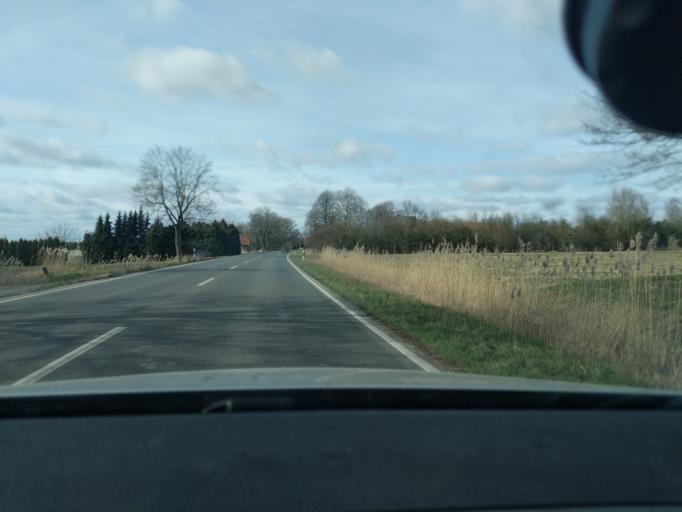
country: DE
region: Lower Saxony
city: Drochtersen
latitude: 53.6955
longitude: 9.4206
